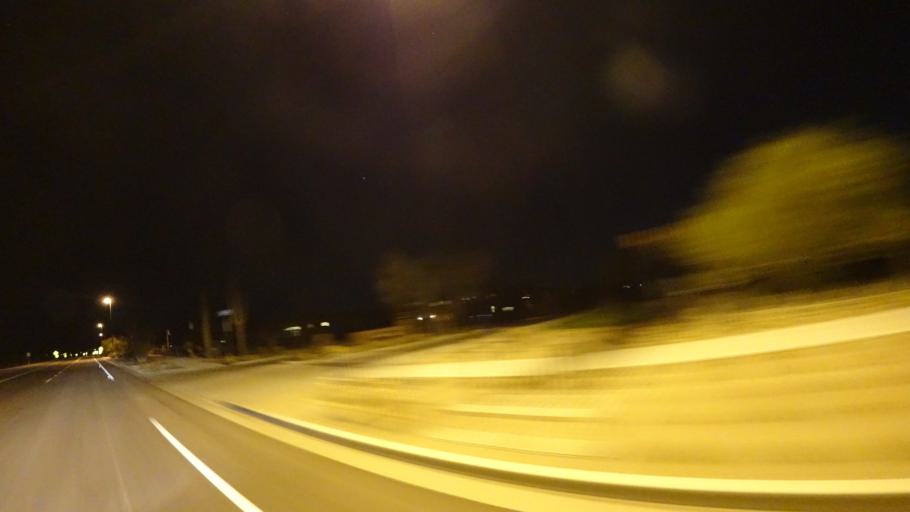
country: US
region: Arizona
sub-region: Pinal County
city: Apache Junction
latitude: 33.4513
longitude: -111.6192
